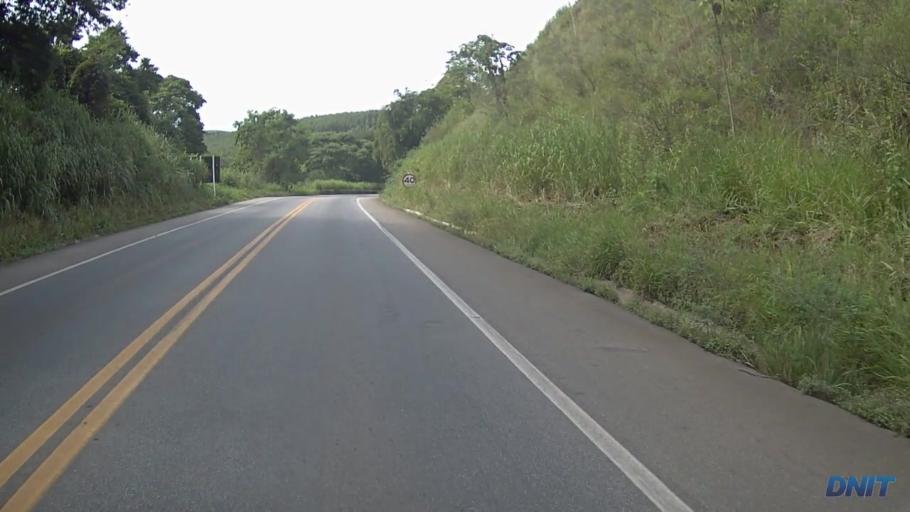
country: BR
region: Minas Gerais
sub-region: Ipaba
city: Ipaba
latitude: -19.3572
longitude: -42.4364
